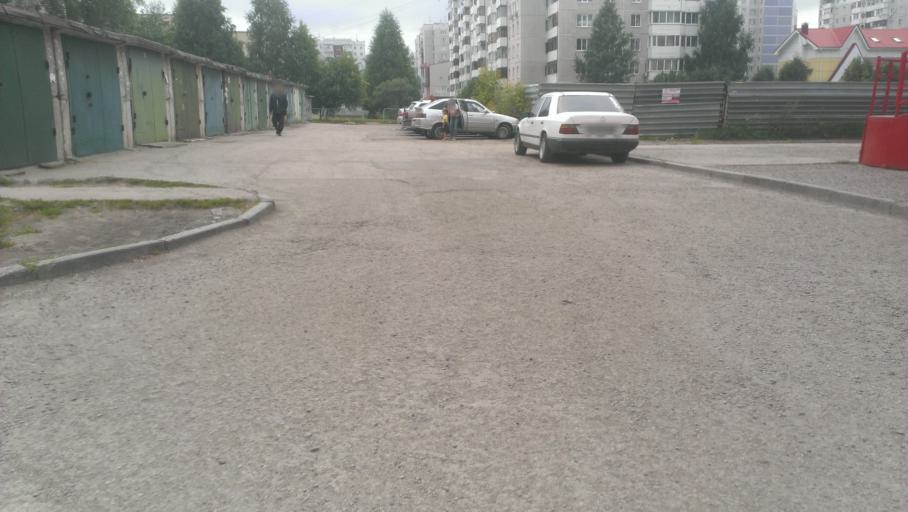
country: RU
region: Altai Krai
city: Novosilikatnyy
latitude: 53.3330
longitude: 83.6833
